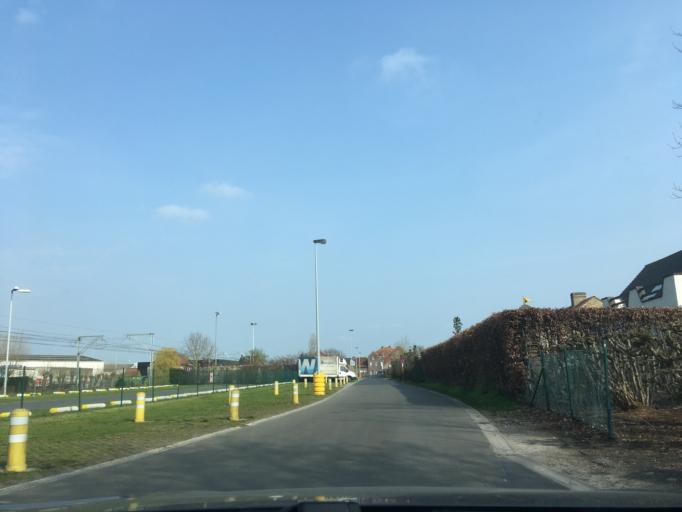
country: BE
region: Flanders
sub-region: Provincie West-Vlaanderen
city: Ardooie
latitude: 50.9897
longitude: 3.2002
